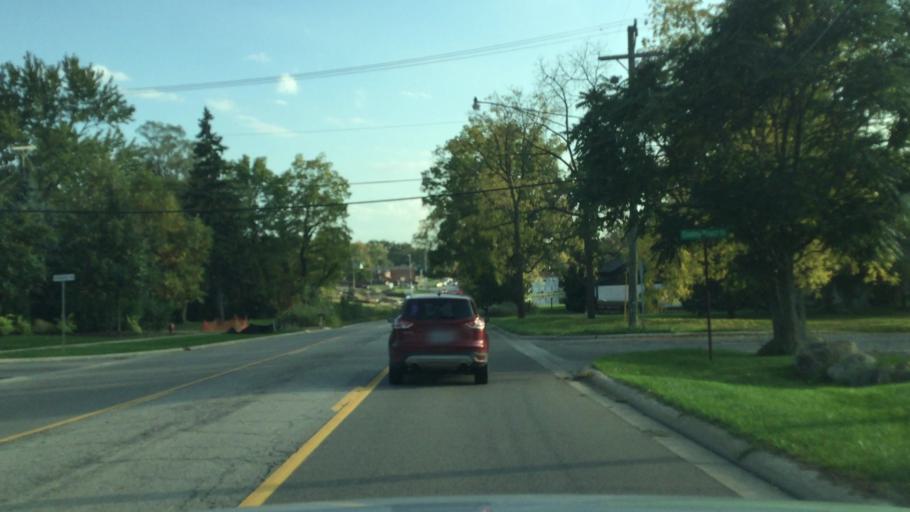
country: US
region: Michigan
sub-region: Oakland County
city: Wolverine Lake
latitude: 42.6173
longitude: -83.4469
